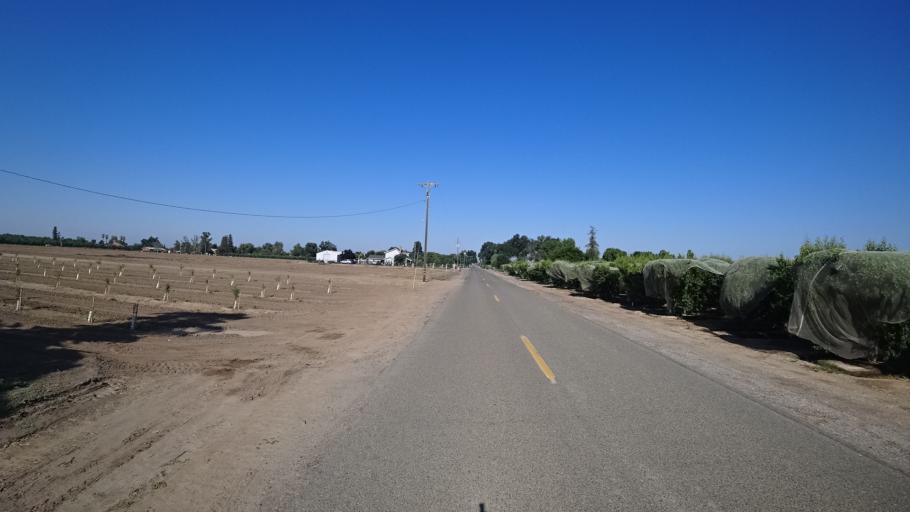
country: US
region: California
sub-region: Kings County
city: Lucerne
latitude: 36.3864
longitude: -119.6502
